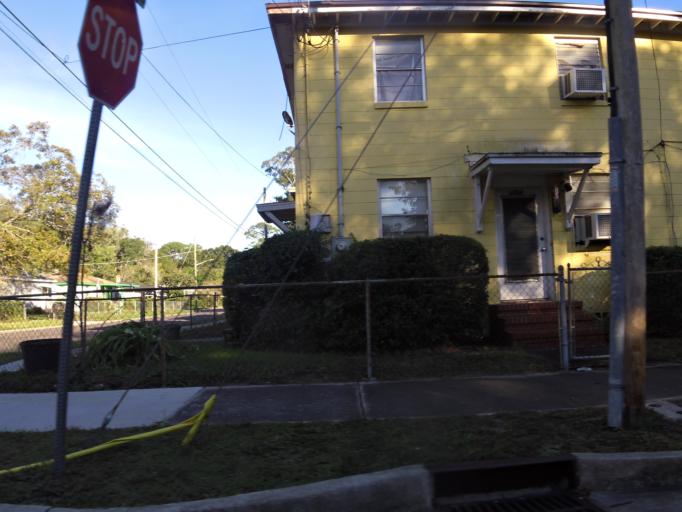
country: US
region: Florida
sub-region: Duval County
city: Jacksonville
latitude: 30.3480
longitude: -81.6820
